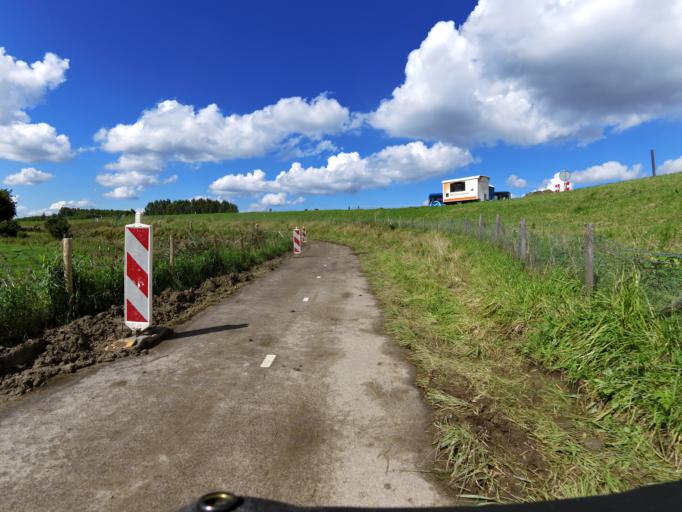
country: NL
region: North Brabant
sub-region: Gemeente Steenbergen
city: Dinteloord
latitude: 51.7015
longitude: 4.3279
